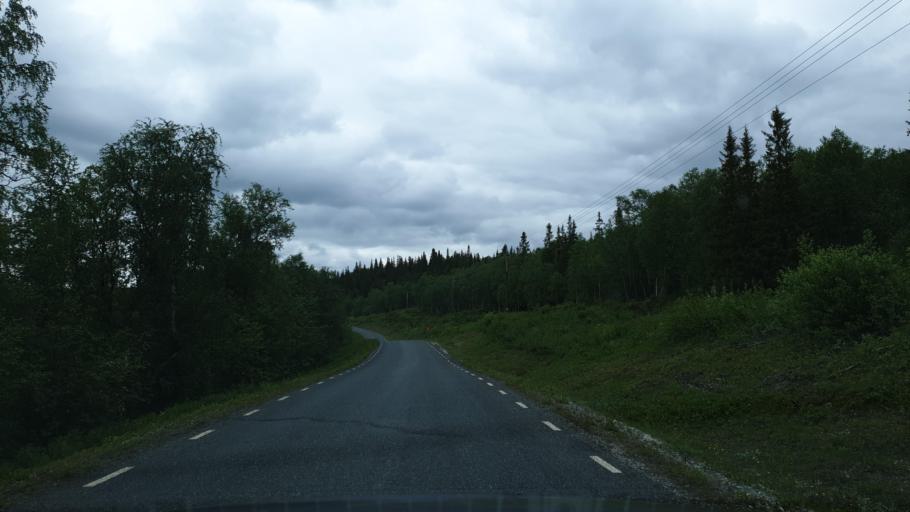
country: SE
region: Vaesterbotten
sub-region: Vilhelmina Kommun
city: Sjoberg
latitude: 65.2915
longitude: 15.2931
